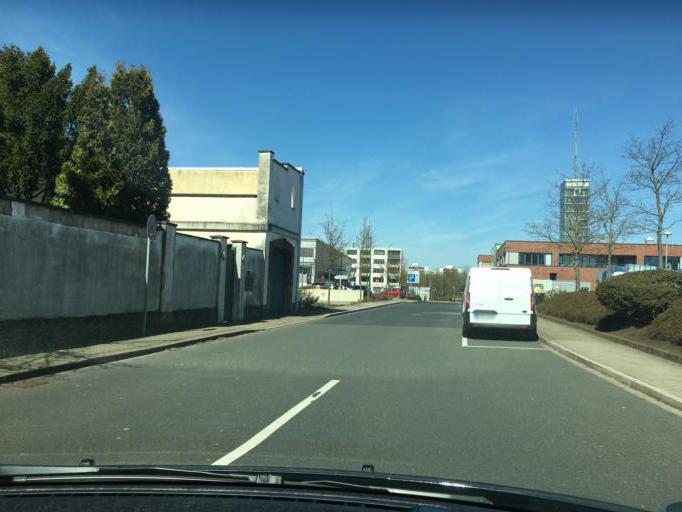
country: DE
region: North Rhine-Westphalia
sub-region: Regierungsbezirk Dusseldorf
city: Ratingen
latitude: 51.2883
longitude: 6.8630
